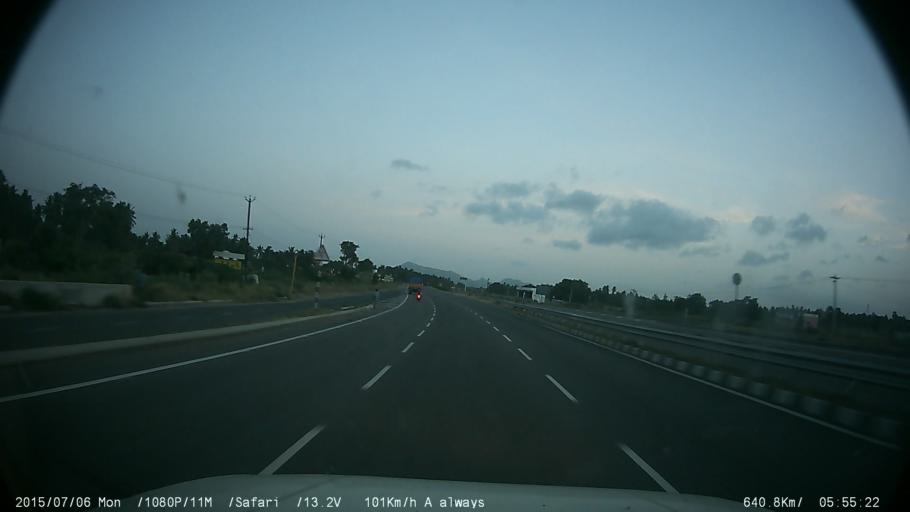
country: IN
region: Tamil Nadu
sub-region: Krishnagiri
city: Krishnagiri
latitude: 12.5622
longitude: 78.1803
